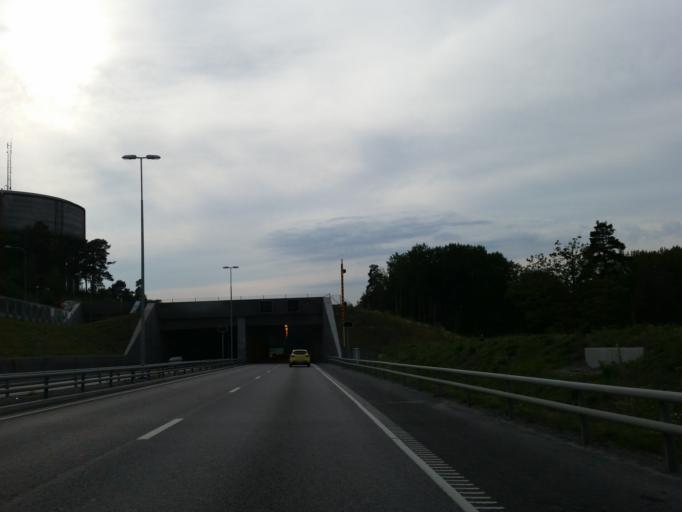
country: SE
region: Stockholm
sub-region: Stockholms Kommun
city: Kista
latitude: 59.3990
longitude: 17.9018
